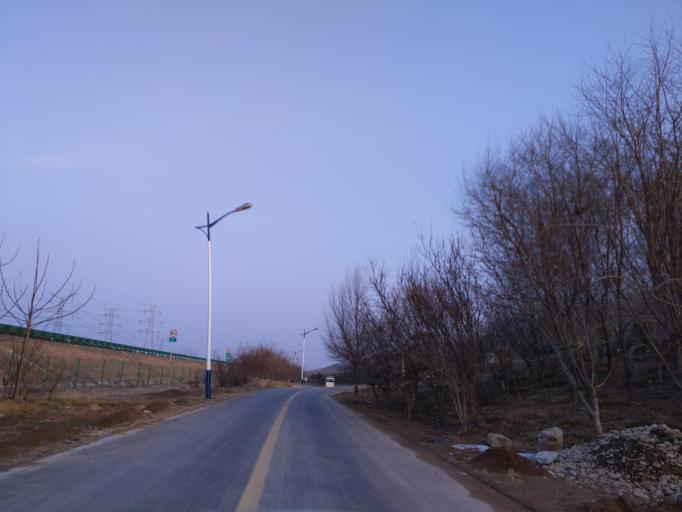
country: CN
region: Henan Sheng
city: Puyang
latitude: 35.8209
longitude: 115.0194
